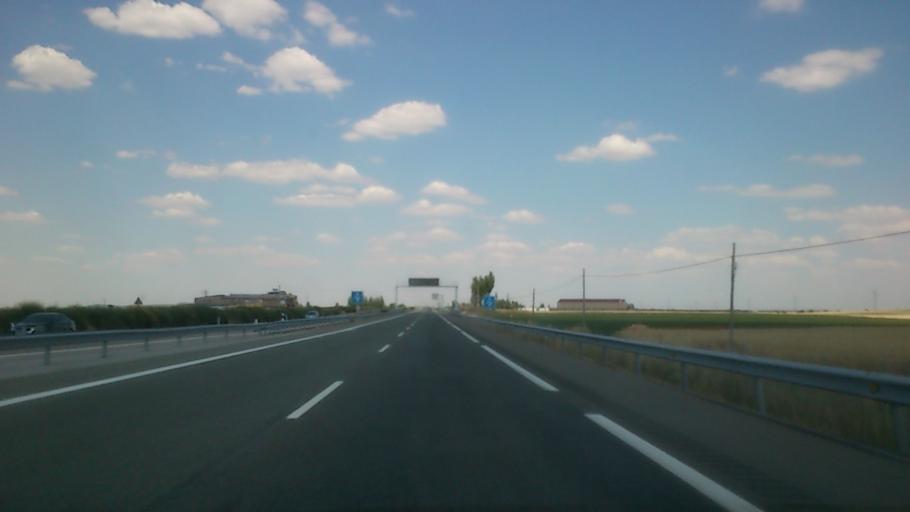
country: ES
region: Castille-La Mancha
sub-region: Provincia de Guadalajara
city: Almadrones
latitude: 40.8902
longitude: -2.7728
